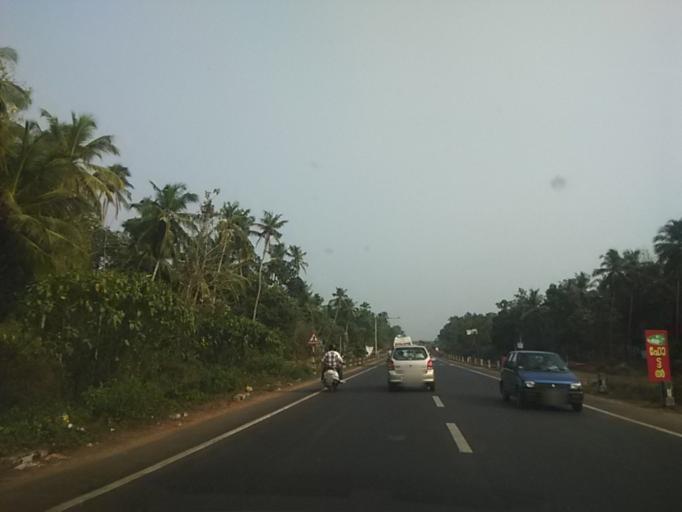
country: IN
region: Kerala
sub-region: Kozhikode
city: Kozhikode
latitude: 11.3061
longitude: 75.7881
